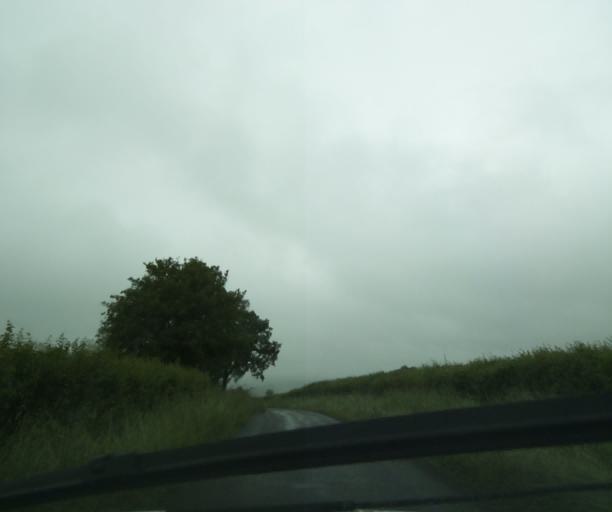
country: FR
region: Bourgogne
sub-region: Departement de Saone-et-Loire
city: Ciry-le-Noble
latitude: 46.5363
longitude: 4.3559
